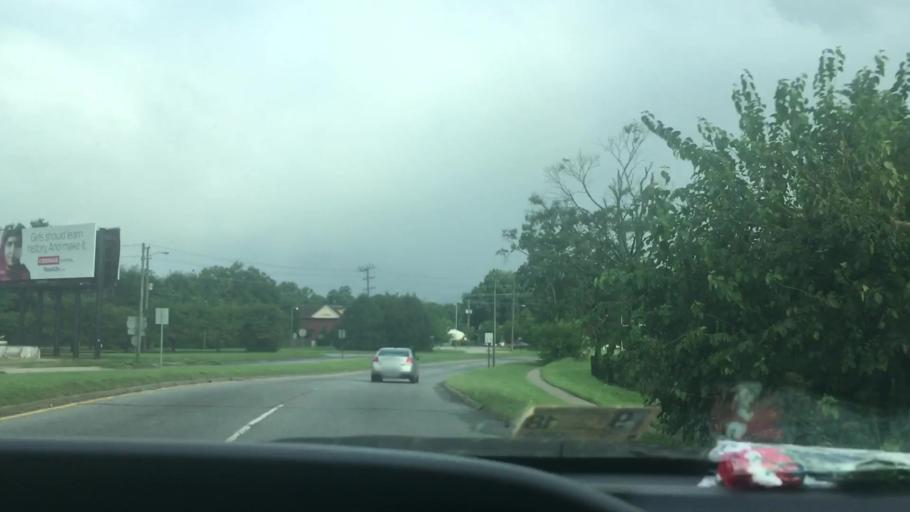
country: US
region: Virginia
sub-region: City of Portsmouth
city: Portsmouth Heights
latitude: 36.8233
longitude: -76.3377
